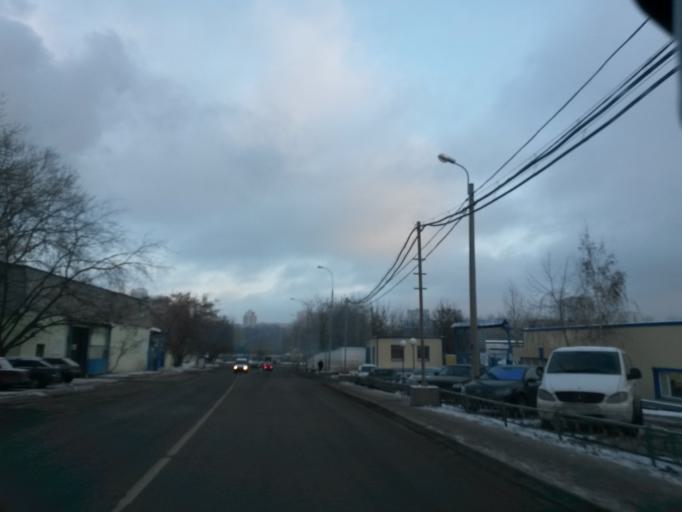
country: RU
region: Moscow
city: Amin'yevo
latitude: 55.7079
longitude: 37.4482
